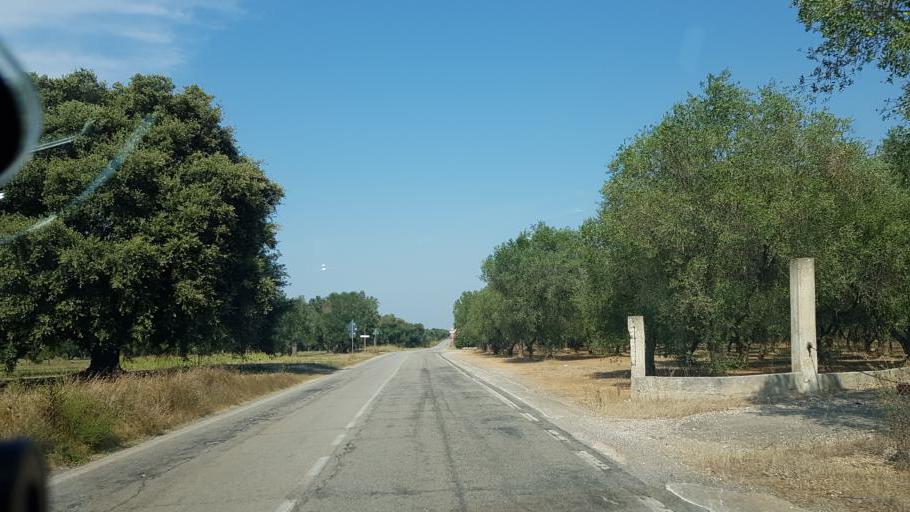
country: IT
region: Apulia
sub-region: Provincia di Brindisi
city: Torre Santa Susanna
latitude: 40.5064
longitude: 17.7713
